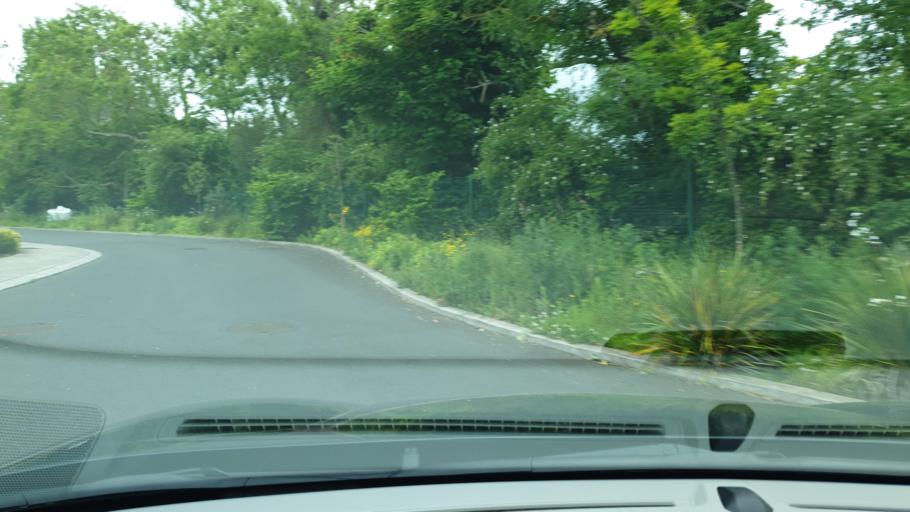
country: IE
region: Leinster
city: Lucan
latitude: 53.3429
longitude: -6.4568
